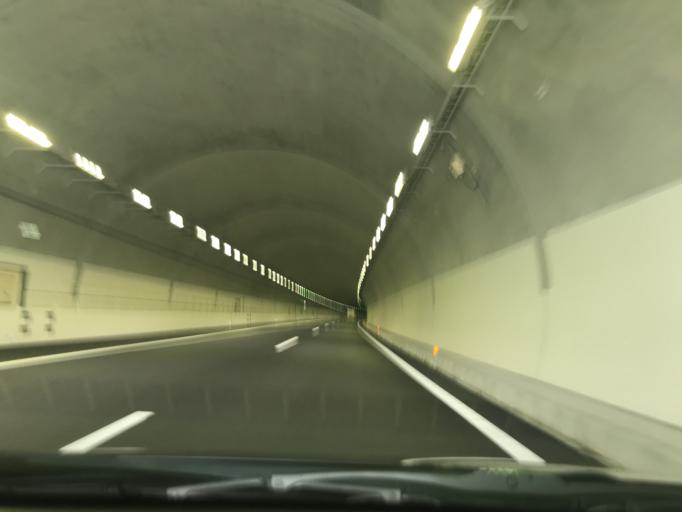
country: JP
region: Osaka
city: Ikeda
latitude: 34.8757
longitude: 135.4194
